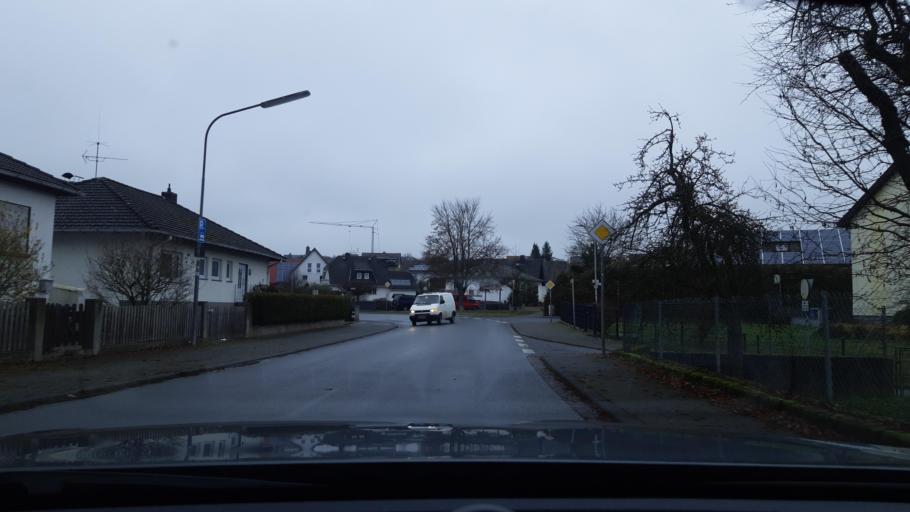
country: DE
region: Hesse
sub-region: Regierungsbezirk Giessen
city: Schoeffengrund
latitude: 50.5012
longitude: 8.5443
